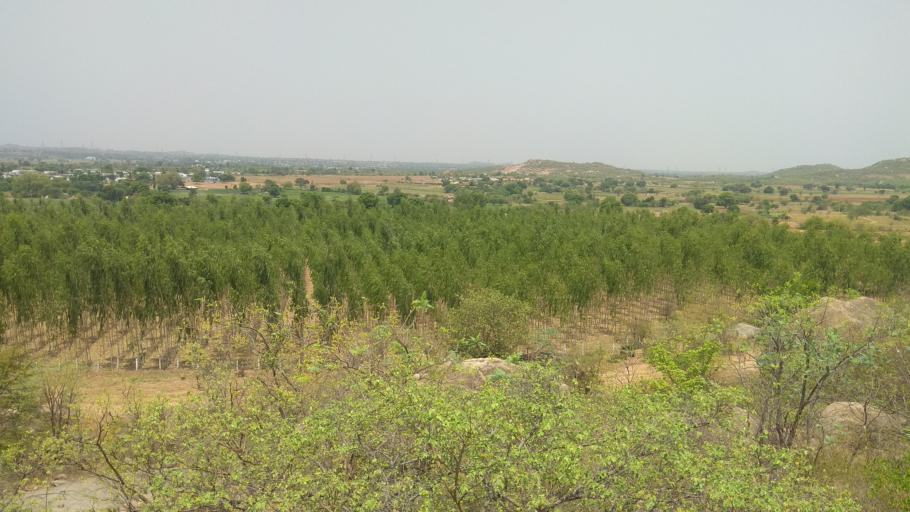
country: IN
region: Telangana
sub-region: Mahbubnagar
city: Farrukhnagar
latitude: 16.8847
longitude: 78.4976
